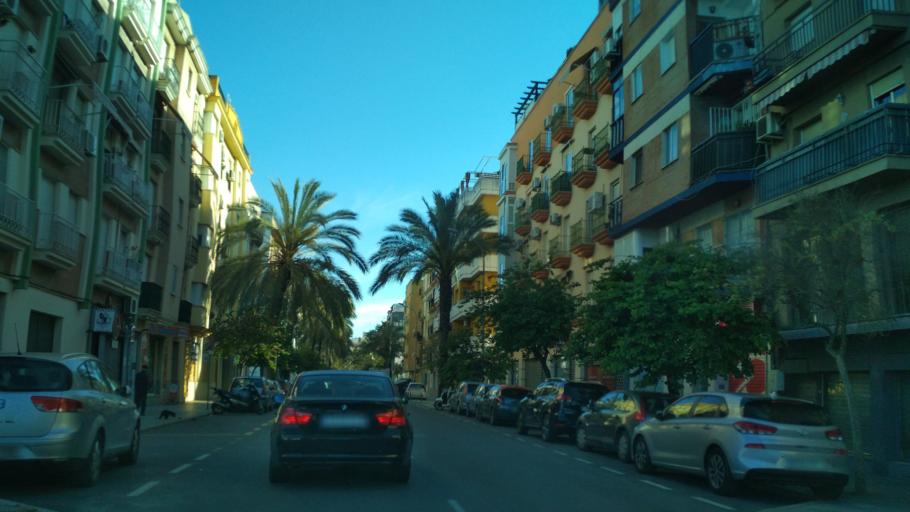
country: ES
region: Andalusia
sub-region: Provincia de Huelva
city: Huelva
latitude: 37.2692
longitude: -6.9513
